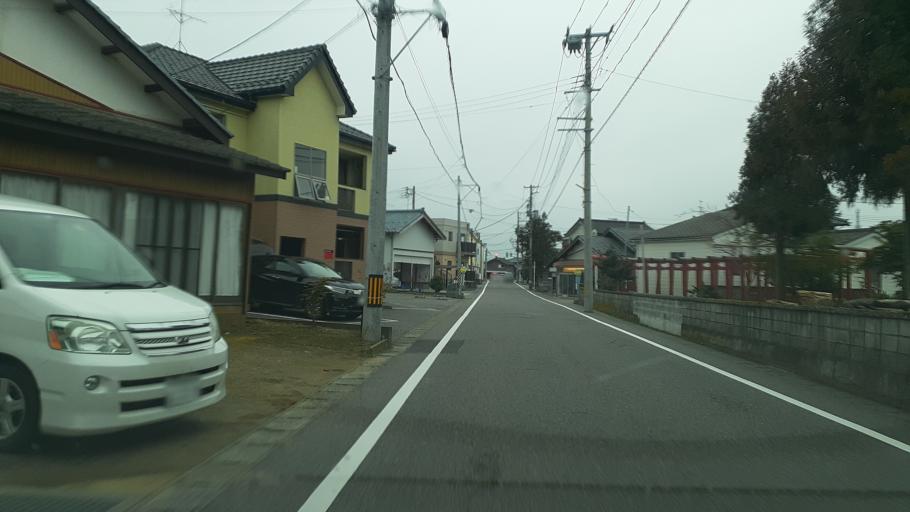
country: JP
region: Niigata
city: Niigata-shi
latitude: 37.8564
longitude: 139.0341
